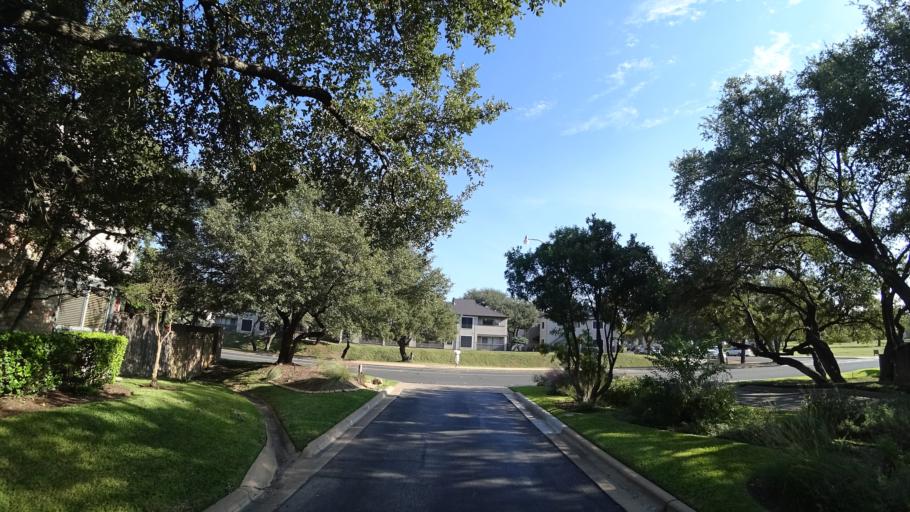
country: US
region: Texas
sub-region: Williamson County
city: Anderson Mill
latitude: 30.4547
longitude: -97.8078
